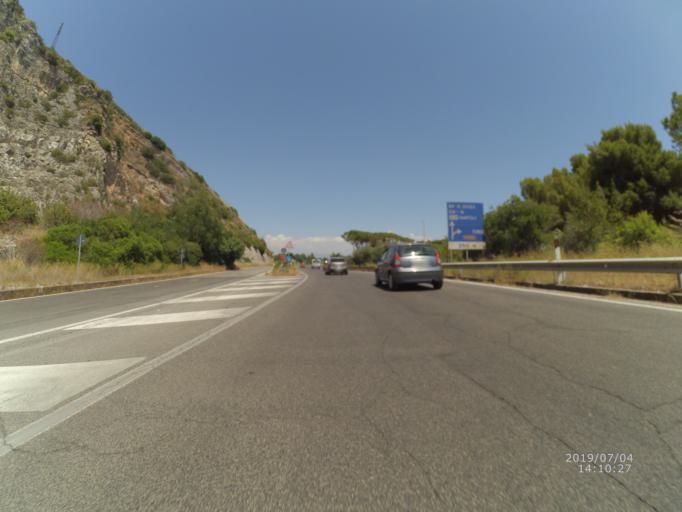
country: IT
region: Latium
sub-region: Provincia di Latina
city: Terracina
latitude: 41.2978
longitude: 13.2756
